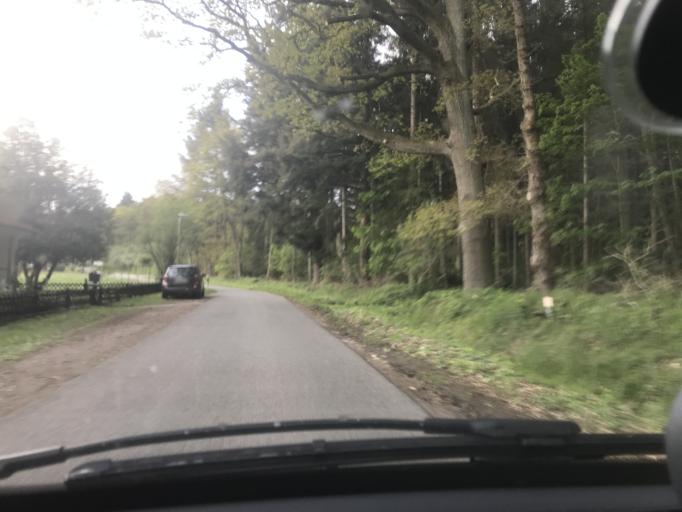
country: DE
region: Lower Saxony
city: Buxtehude
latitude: 53.4523
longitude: 9.7330
